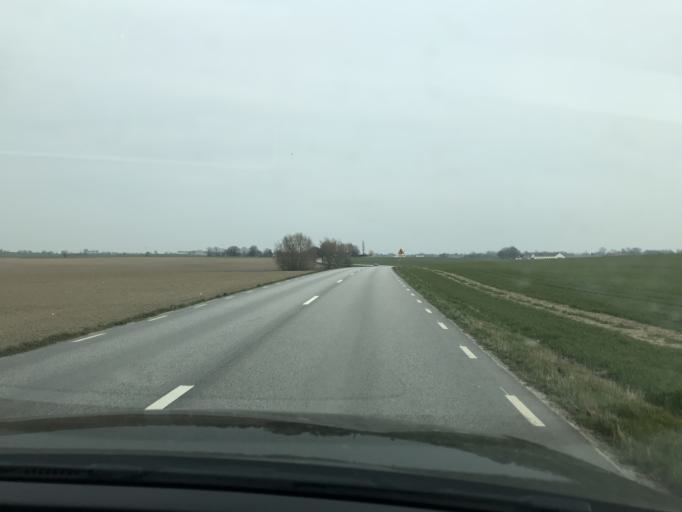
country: SE
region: Skane
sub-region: Skurups Kommun
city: Skivarp
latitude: 55.4251
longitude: 13.5897
